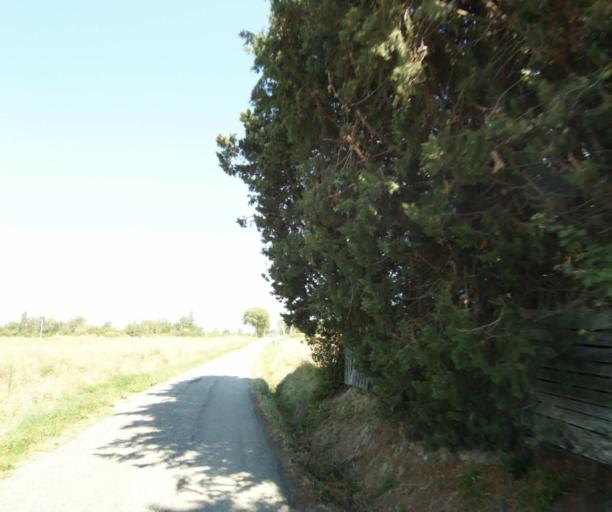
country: FR
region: Midi-Pyrenees
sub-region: Departement de l'Ariege
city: Lezat-sur-Leze
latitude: 43.2820
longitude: 1.3555
